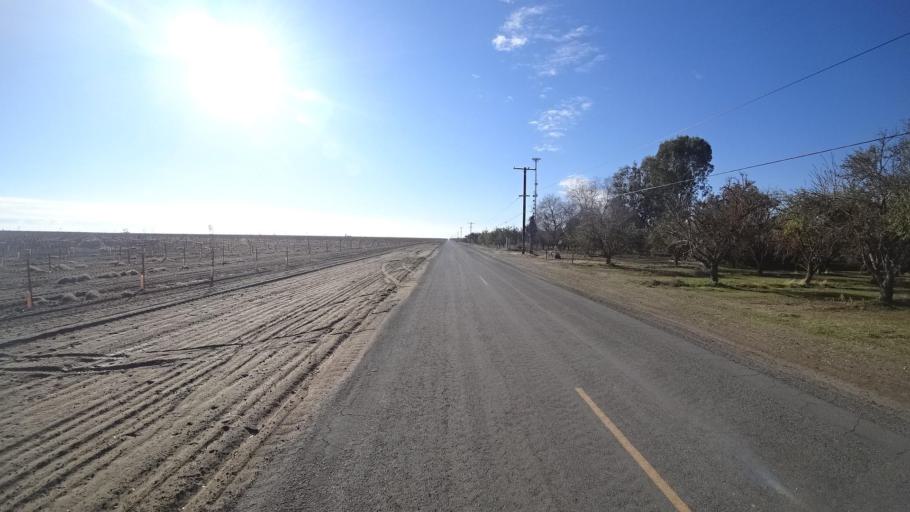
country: US
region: California
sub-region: Kern County
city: Delano
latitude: 35.7564
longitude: -119.3119
